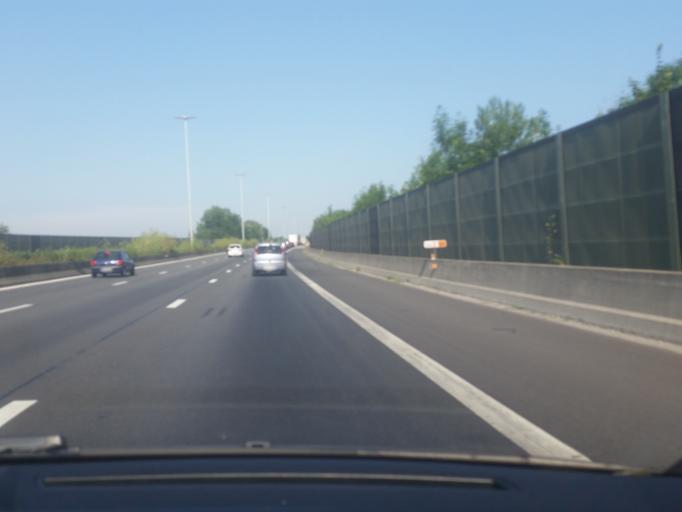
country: BE
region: Flanders
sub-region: Provincie Oost-Vlaanderen
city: Haaltert
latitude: 50.9265
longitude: 3.9659
